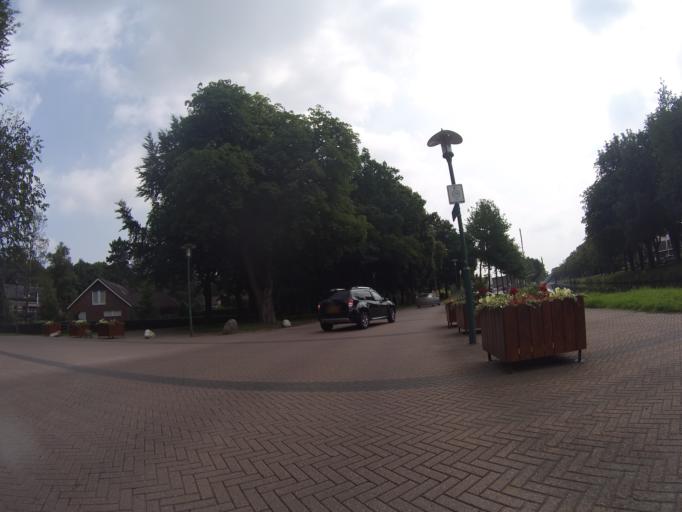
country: NL
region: Drenthe
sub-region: Gemeente Emmen
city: Emmer-Compascuum
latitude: 52.8737
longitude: 7.0723
